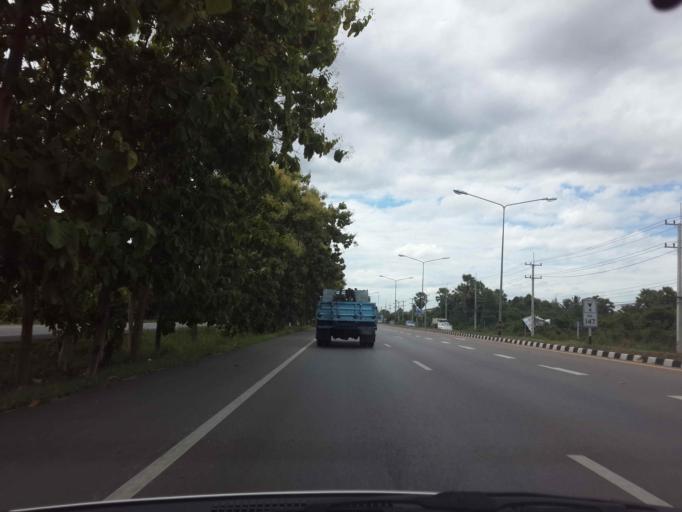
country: TH
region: Phetchaburi
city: Khao Yoi
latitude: 13.1528
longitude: 99.8507
